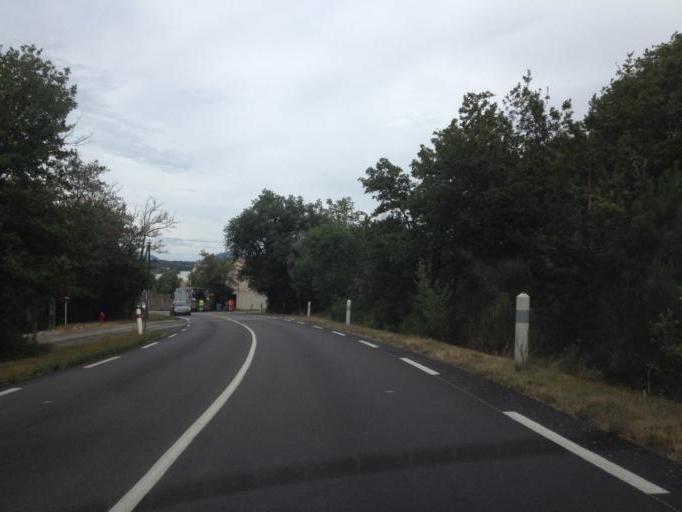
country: FR
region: Rhone-Alpes
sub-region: Departement de la Drome
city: Montelimar
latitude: 44.5311
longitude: 4.7677
